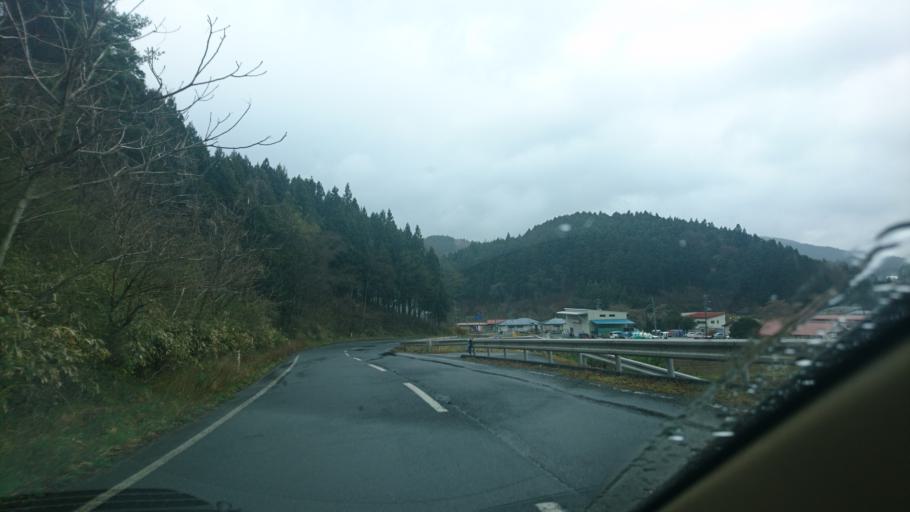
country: JP
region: Iwate
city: Ofunato
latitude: 38.9400
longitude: 141.4609
